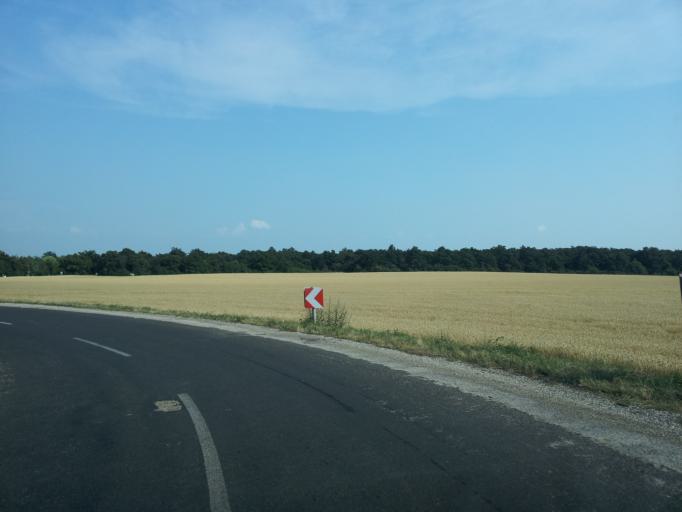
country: HU
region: Veszprem
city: Csopak
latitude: 47.0216
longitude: 17.9073
